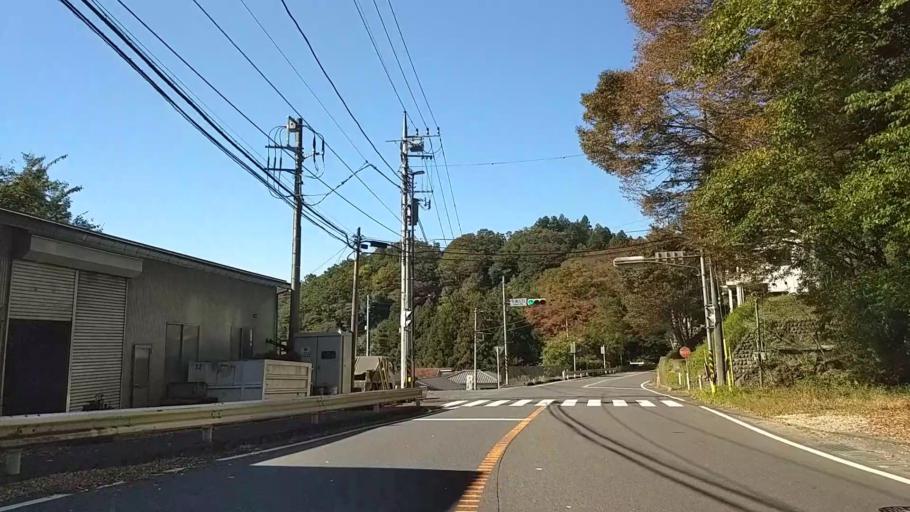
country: JP
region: Yamanashi
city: Uenohara
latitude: 35.6184
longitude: 139.1346
